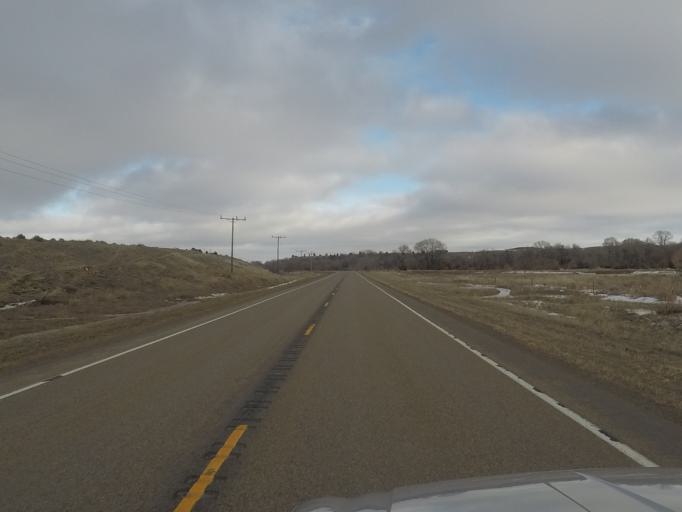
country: US
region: Montana
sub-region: Golden Valley County
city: Ryegate
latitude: 46.2987
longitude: -109.3146
